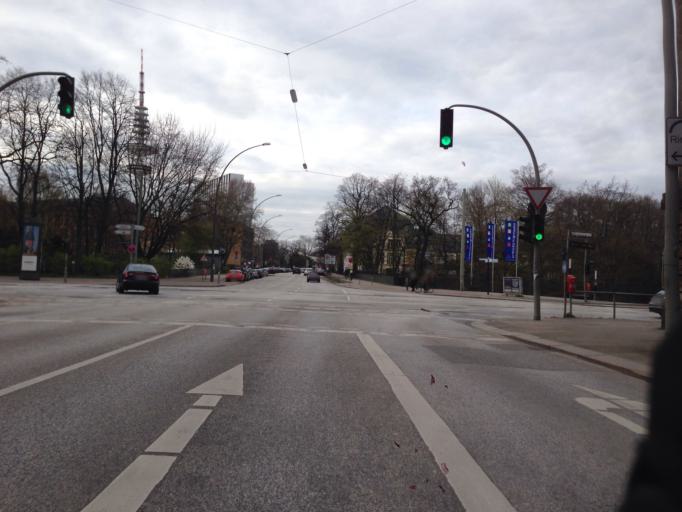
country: DE
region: Hamburg
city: Neustadt
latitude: 53.5573
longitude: 9.9840
